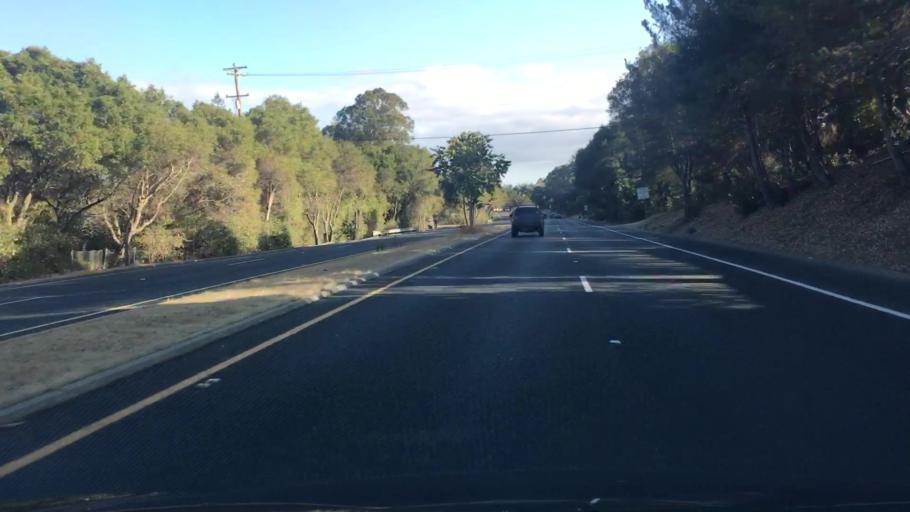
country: US
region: California
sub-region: Santa Clara County
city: Los Altos Hills
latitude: 37.3904
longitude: -122.1282
